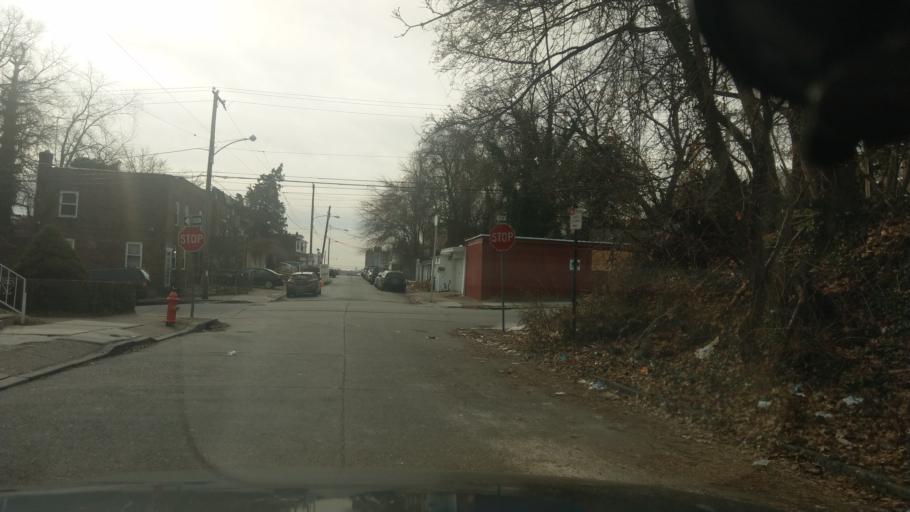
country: US
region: Pennsylvania
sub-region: Montgomery County
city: Wyncote
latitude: 40.0440
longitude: -75.1374
